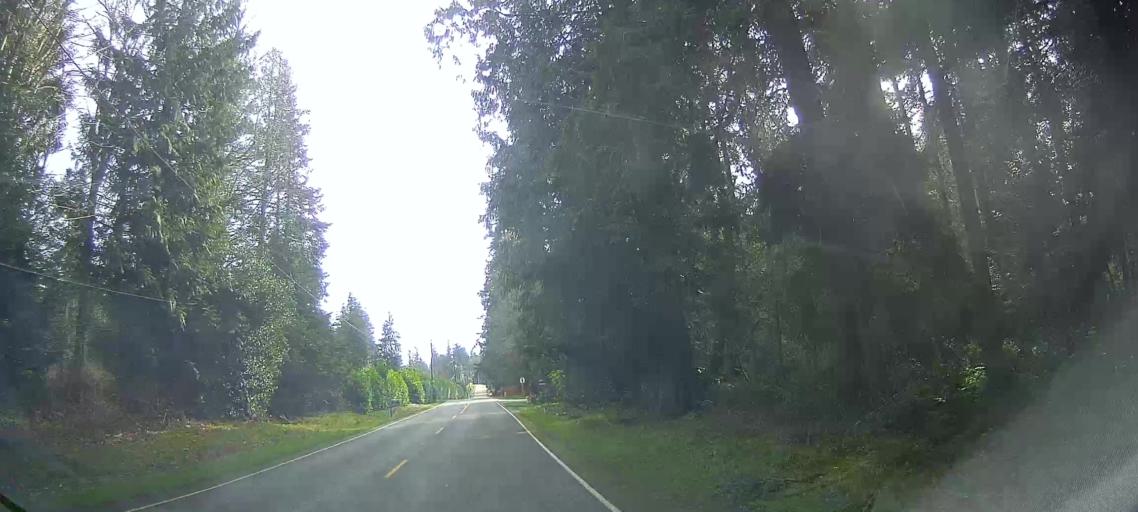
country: US
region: Washington
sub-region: Island County
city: Langley
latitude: 48.0986
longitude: -122.4149
